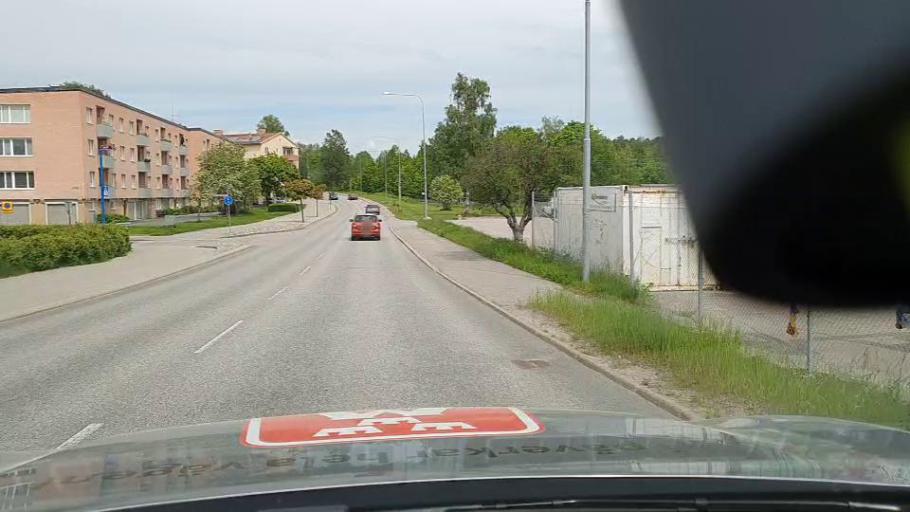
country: SE
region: Soedermanland
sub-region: Flens Kommun
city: Flen
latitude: 59.0535
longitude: 16.5953
